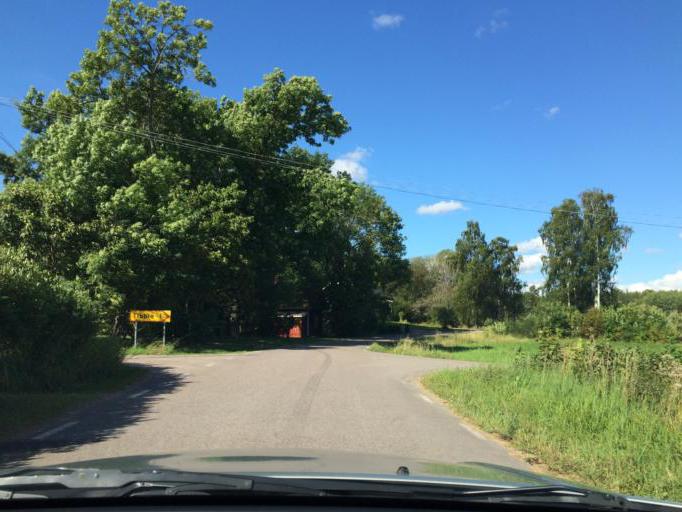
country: SE
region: Soedermanland
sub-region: Eskilstuna Kommun
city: Kvicksund
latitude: 59.4955
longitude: 16.3325
